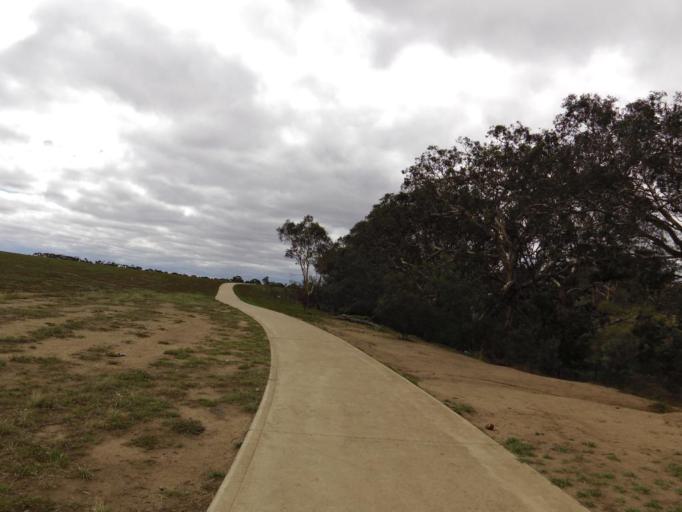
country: AU
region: Victoria
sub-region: Wyndham
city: Tarneit
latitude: -37.8831
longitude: 144.6401
